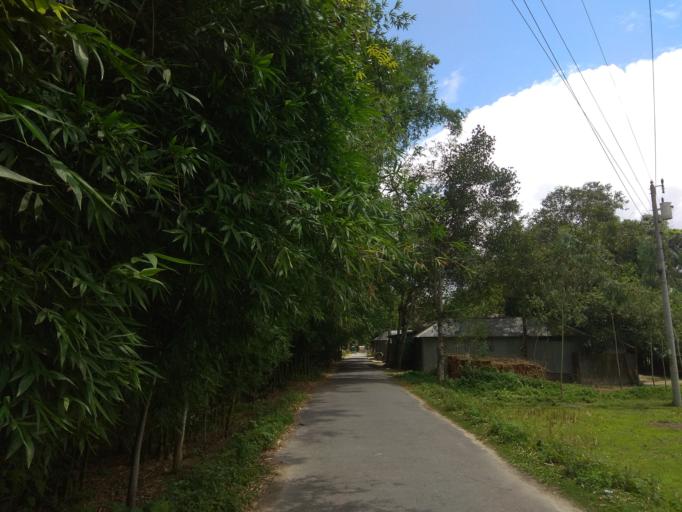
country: IN
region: West Bengal
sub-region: Koch Bihar
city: Haldibari
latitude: 26.1620
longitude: 88.9245
